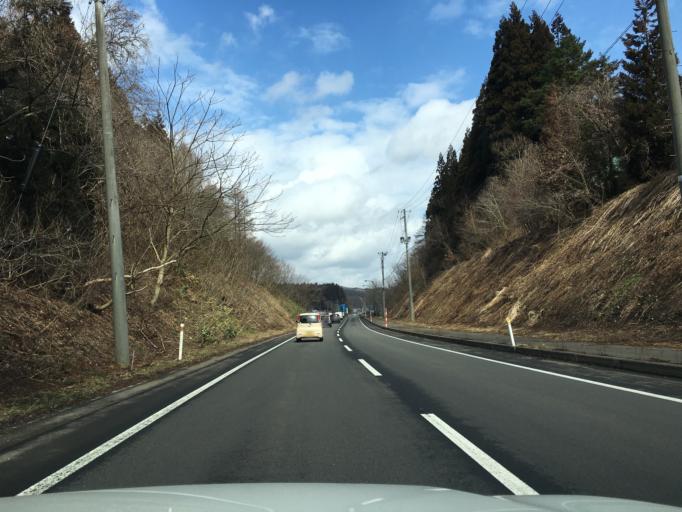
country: JP
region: Akita
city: Takanosu
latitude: 40.0281
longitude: 140.2738
